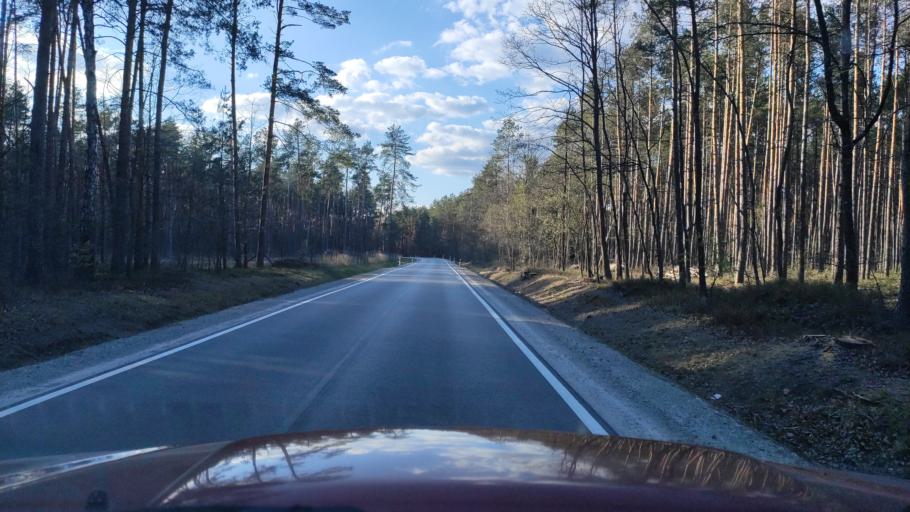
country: PL
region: Masovian Voivodeship
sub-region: Powiat zwolenski
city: Zwolen
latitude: 51.4016
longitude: 21.5367
